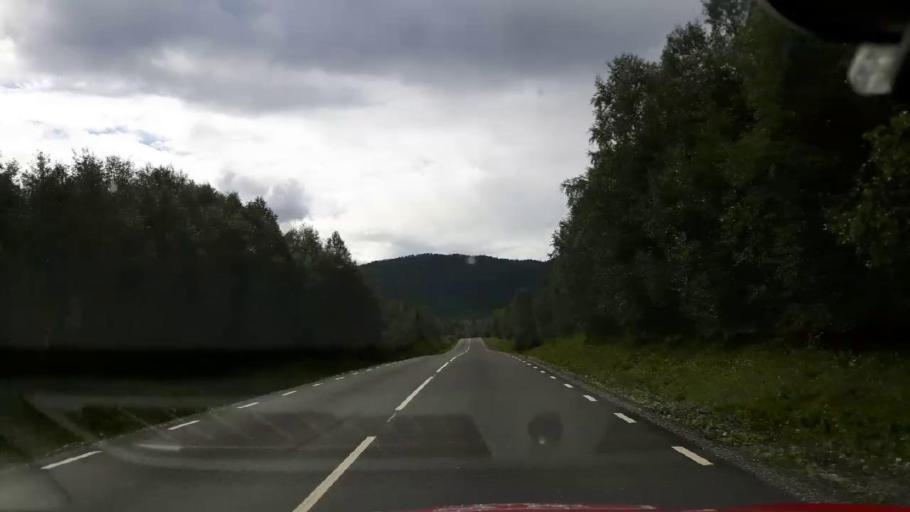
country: NO
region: Nord-Trondelag
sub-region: Royrvik
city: Royrvik
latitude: 64.8927
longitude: 14.1907
